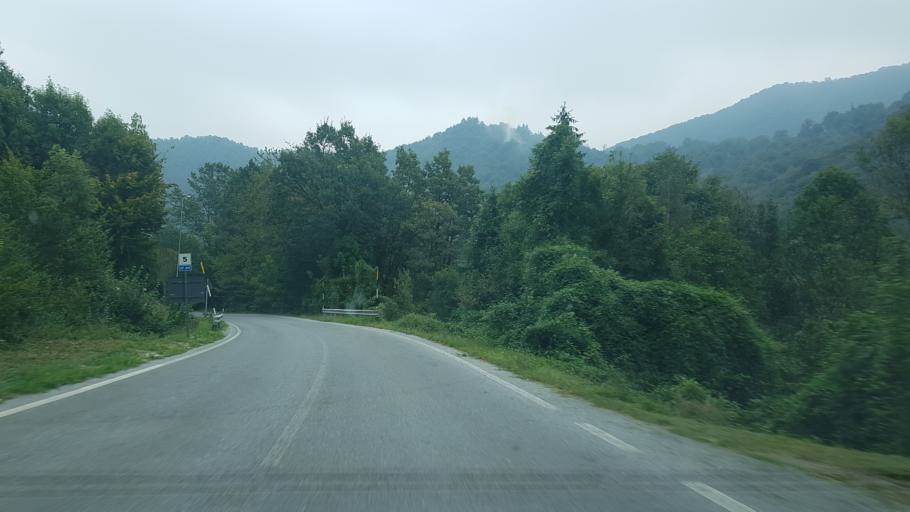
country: IT
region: Piedmont
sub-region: Provincia di Cuneo
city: Roccaforte Mondovi
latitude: 44.2760
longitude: 7.7405
